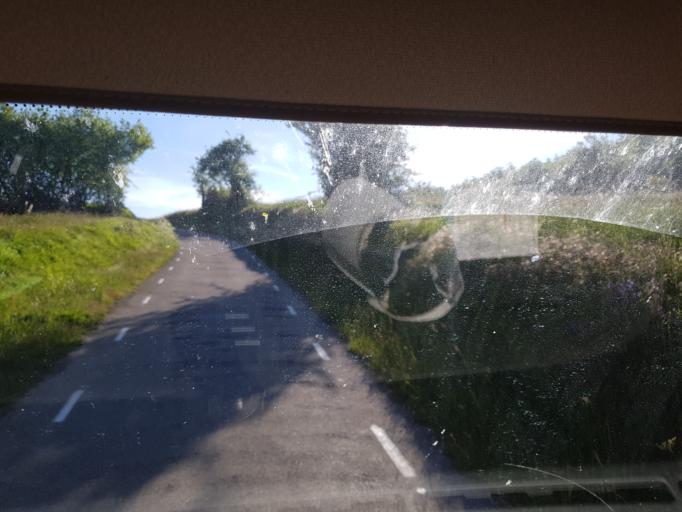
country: ES
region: Cantabria
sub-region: Provincia de Cantabria
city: San Martin de Elines
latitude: 42.9558
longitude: -3.7995
